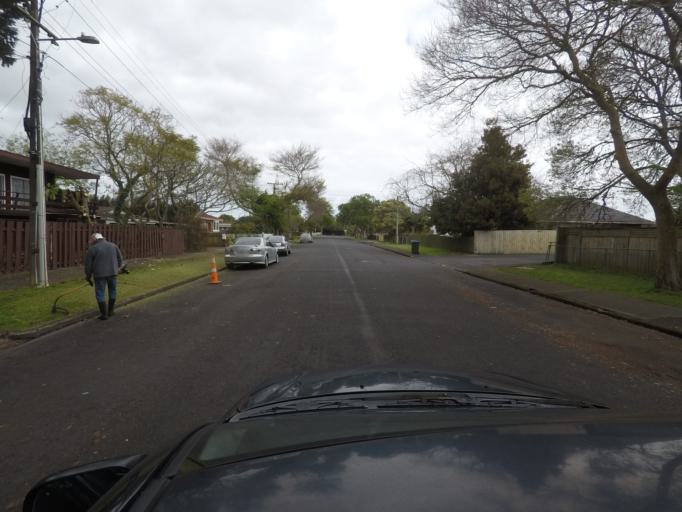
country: NZ
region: Auckland
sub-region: Auckland
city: Tamaki
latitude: -36.9405
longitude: 174.8566
